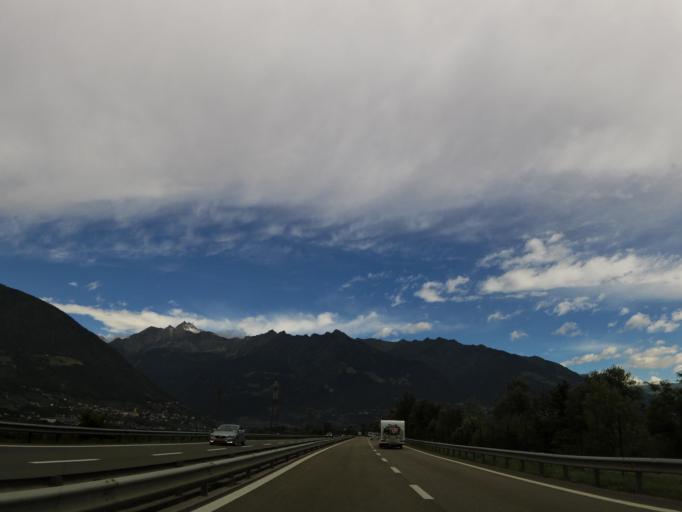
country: IT
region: Trentino-Alto Adige
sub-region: Bolzano
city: Sinigo
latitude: 46.6348
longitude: 11.1717
